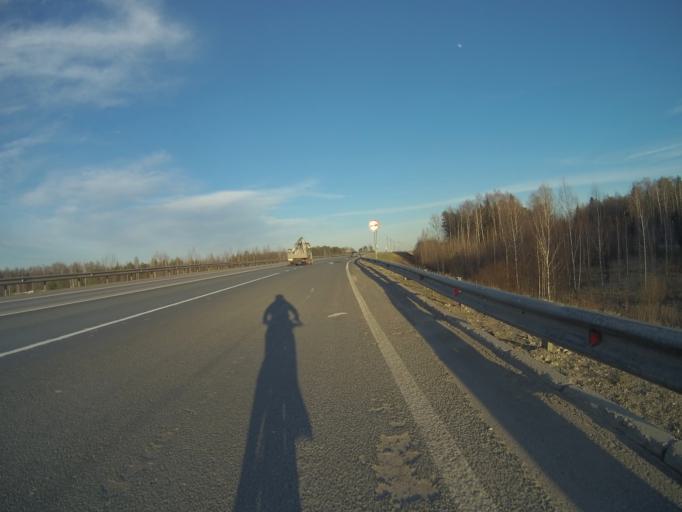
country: RU
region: Vladimir
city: Raduzhnyy
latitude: 56.0647
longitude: 40.3634
